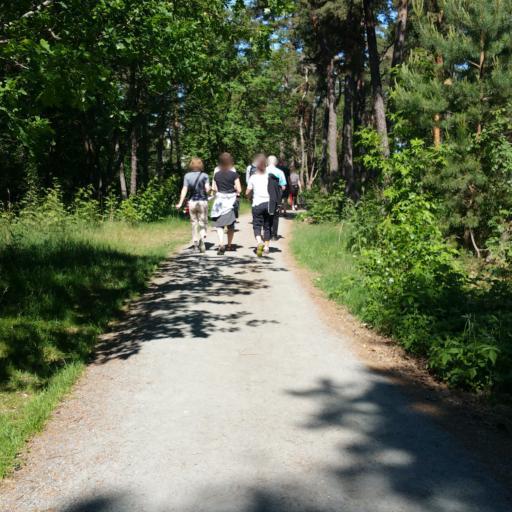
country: SE
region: Uppsala
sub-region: Uppsala Kommun
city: Uppsala
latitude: 59.8464
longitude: 17.6448
